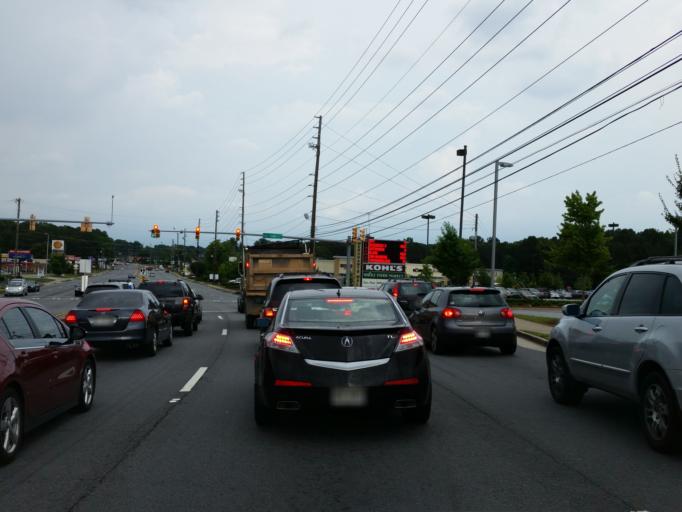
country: US
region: Georgia
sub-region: Fulton County
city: Sandy Springs
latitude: 33.9811
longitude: -84.4260
